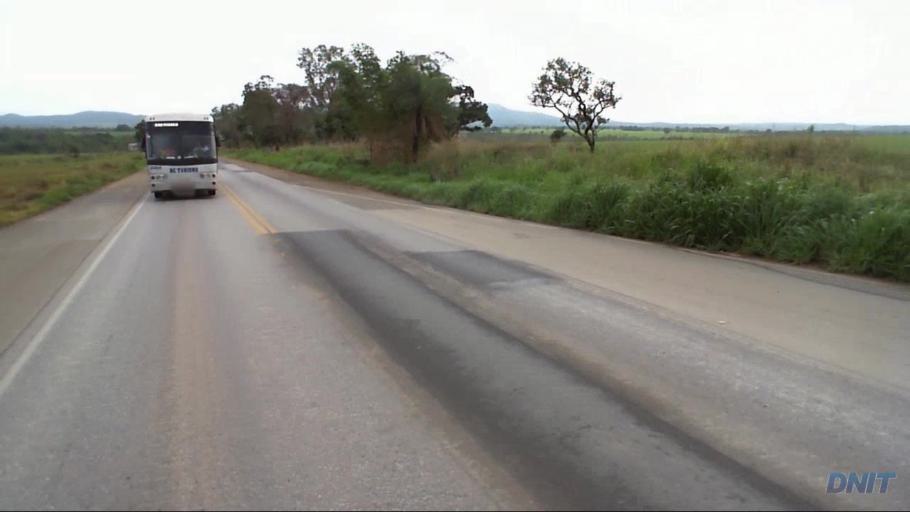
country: BR
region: Goias
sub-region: Uruacu
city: Uruacu
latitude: -14.6219
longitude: -49.1717
